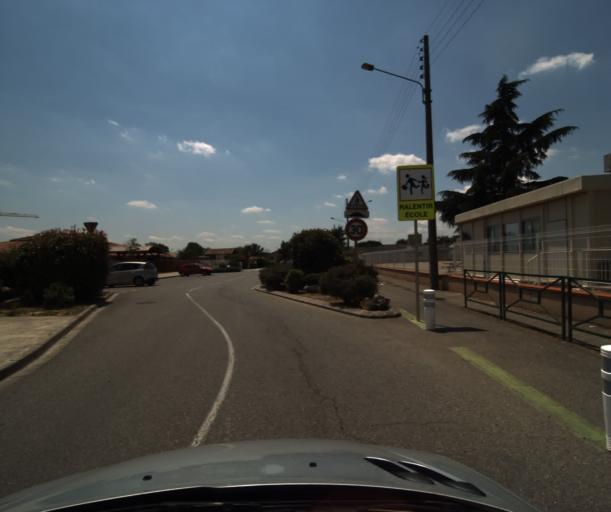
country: FR
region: Midi-Pyrenees
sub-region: Departement de la Haute-Garonne
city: Saint-Lys
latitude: 43.5115
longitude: 1.1811
